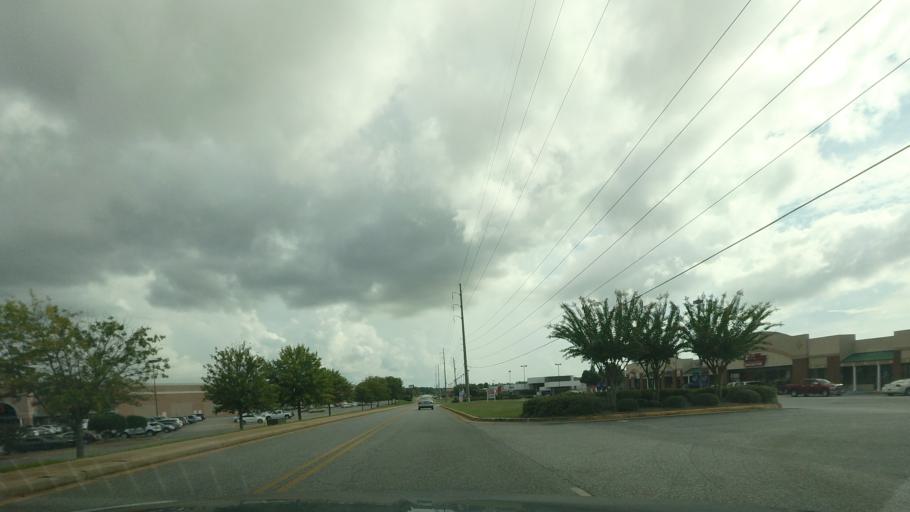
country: US
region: Georgia
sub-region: Houston County
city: Centerville
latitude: 32.6225
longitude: -83.6898
